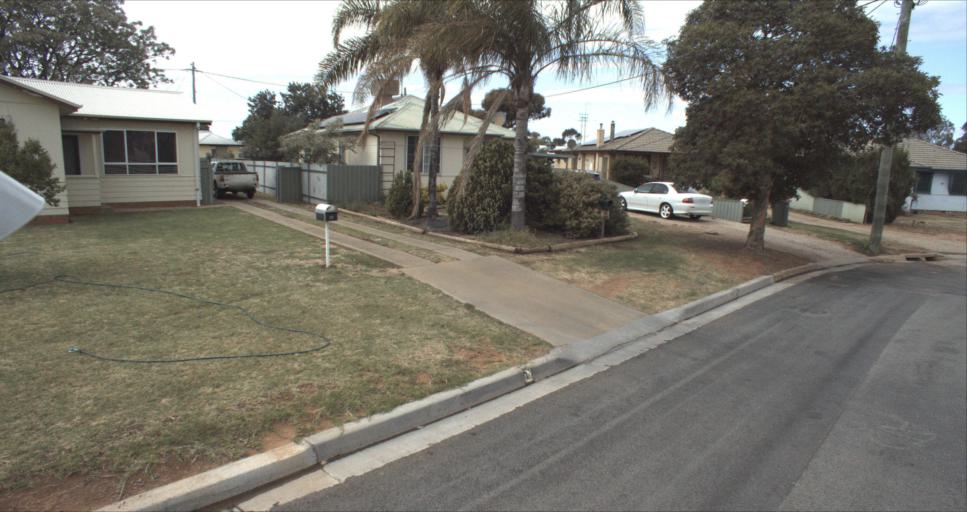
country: AU
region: New South Wales
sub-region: Leeton
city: Leeton
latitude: -34.5660
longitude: 146.3945
